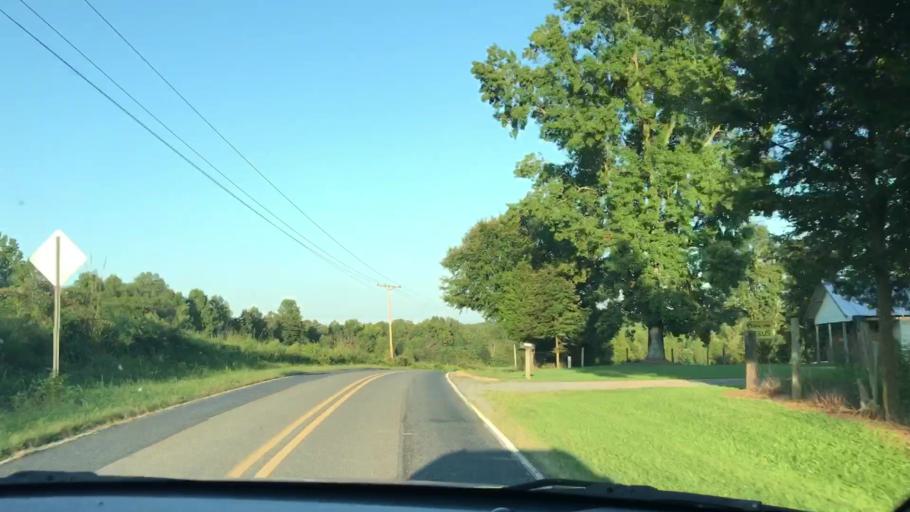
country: US
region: North Carolina
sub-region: Randolph County
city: Franklinville
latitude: 35.8005
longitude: -79.6747
